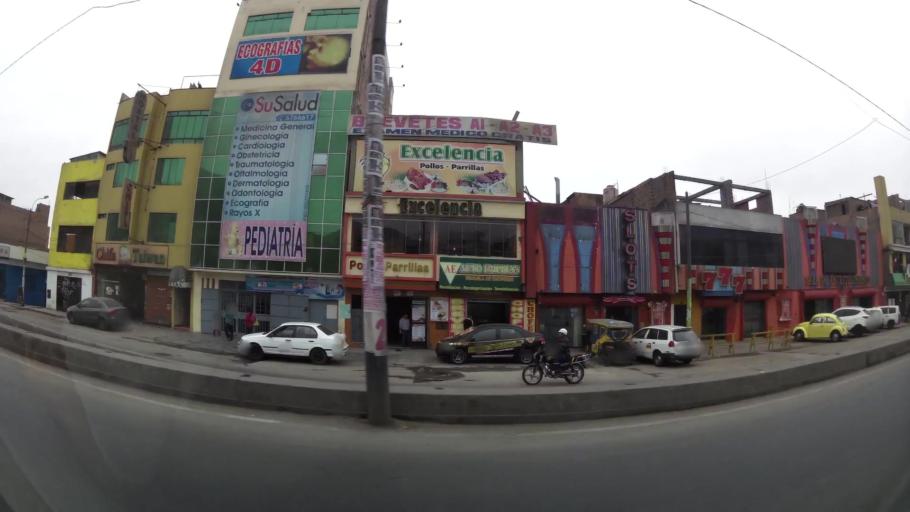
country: PE
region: Lima
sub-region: Lima
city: Independencia
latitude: -11.9587
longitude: -77.0534
